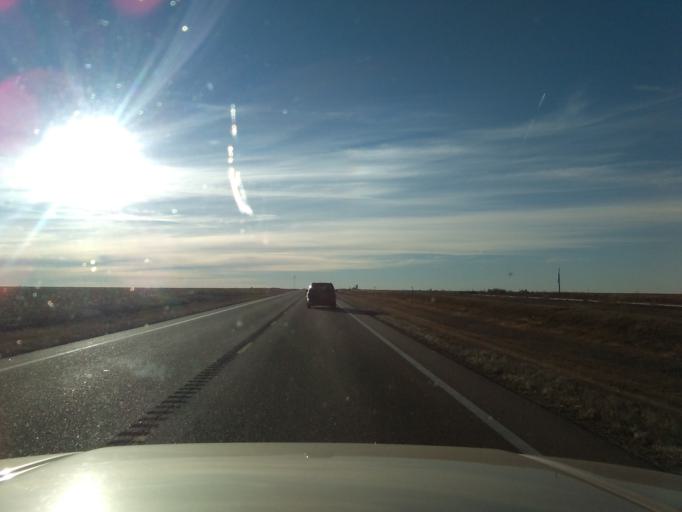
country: US
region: Kansas
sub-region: Thomas County
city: Colby
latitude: 39.4631
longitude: -100.7682
